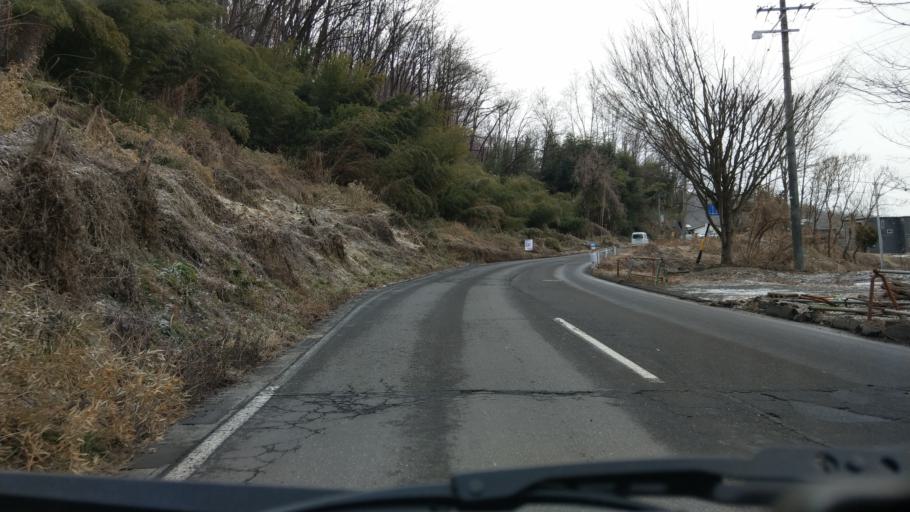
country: JP
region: Nagano
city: Kamimaruko
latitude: 36.3283
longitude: 138.3469
